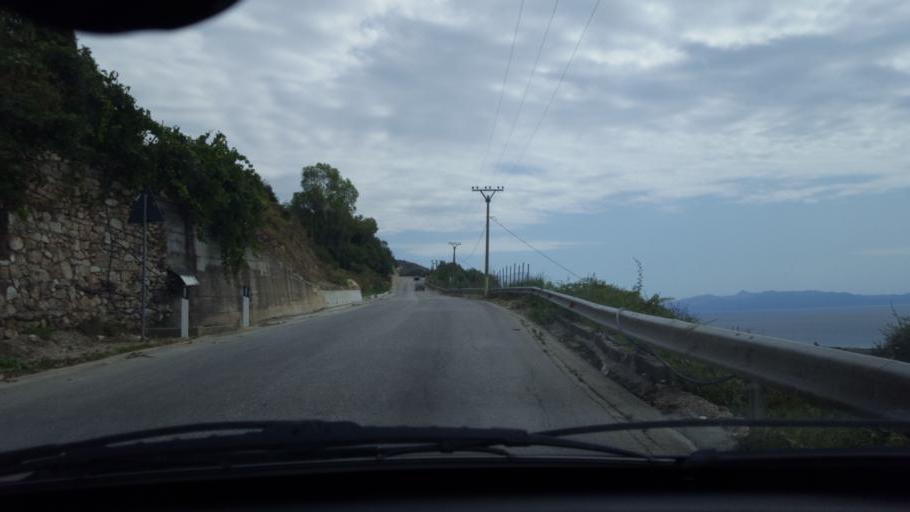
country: AL
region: Vlore
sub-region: Rrethi i Sarandes
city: Lukove
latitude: 40.0604
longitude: 19.8583
